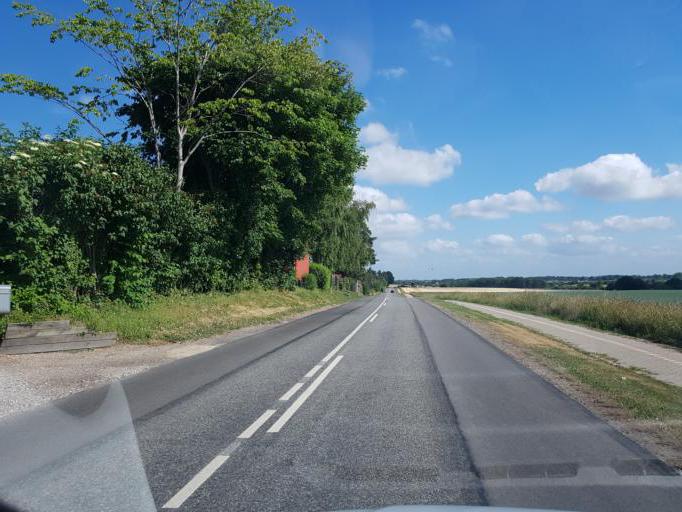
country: DK
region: Zealand
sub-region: Lejre Kommune
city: Osted
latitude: 55.5790
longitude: 11.9674
